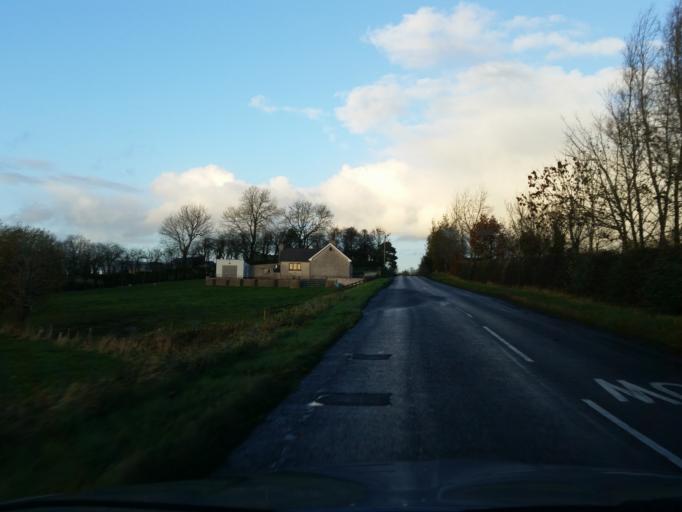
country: GB
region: Northern Ireland
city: Lisnaskea
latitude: 54.2378
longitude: -7.4519
